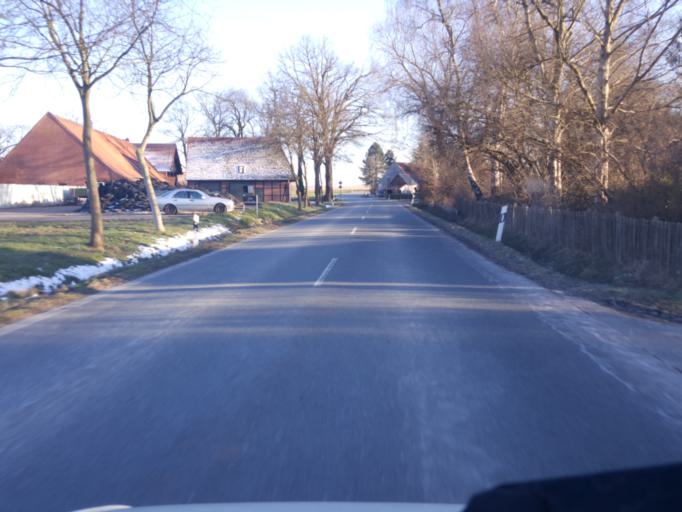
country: DE
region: North Rhine-Westphalia
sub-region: Regierungsbezirk Detmold
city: Hille
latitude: 52.3552
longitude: 8.7310
